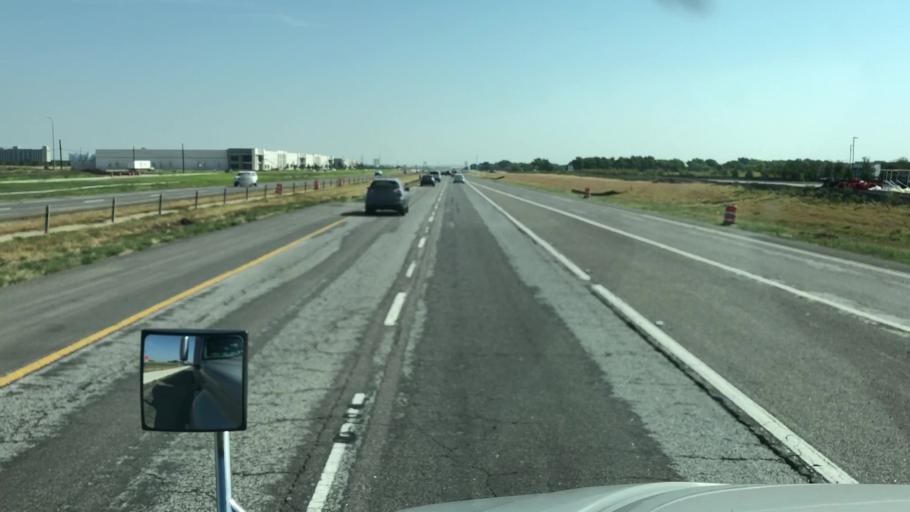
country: US
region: Texas
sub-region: Tarrant County
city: Haslet
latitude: 33.0040
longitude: -97.2903
